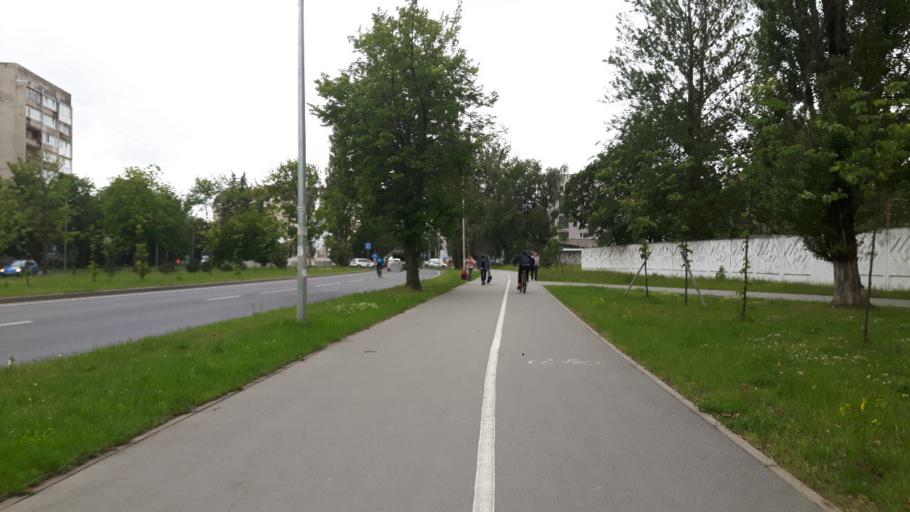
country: RU
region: Kaliningrad
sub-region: Gorod Kaliningrad
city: Kaliningrad
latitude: 54.7325
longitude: 20.4909
